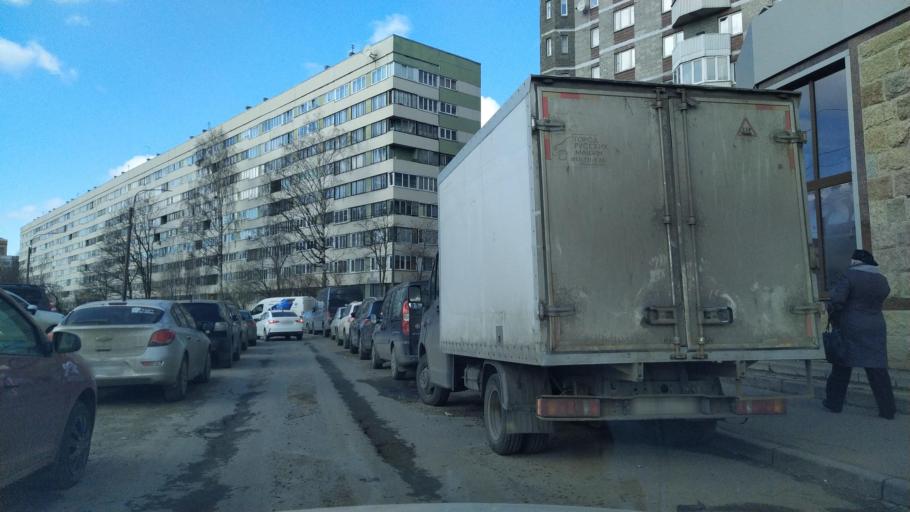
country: RU
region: St.-Petersburg
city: Komendantsky aerodrom
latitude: 60.0055
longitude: 30.2934
